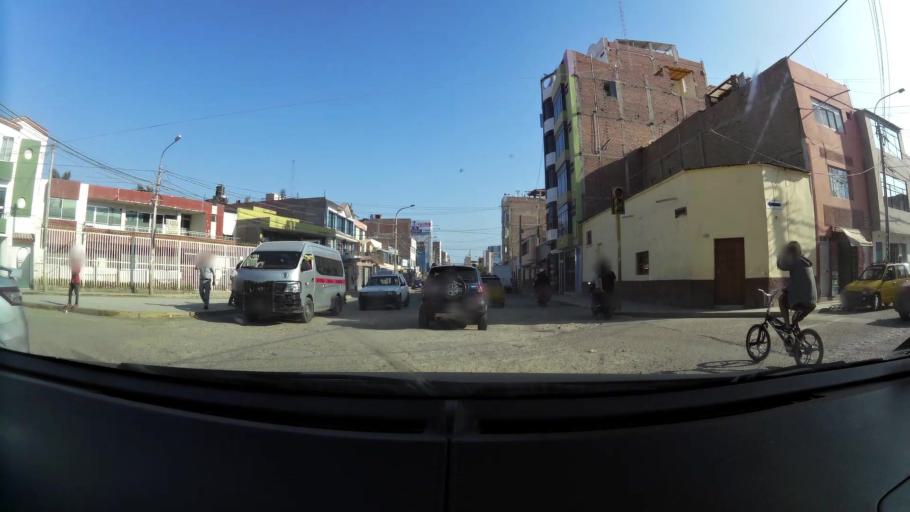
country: PE
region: Lambayeque
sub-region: Provincia de Chiclayo
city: Santa Rosa
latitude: -6.7670
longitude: -79.8355
